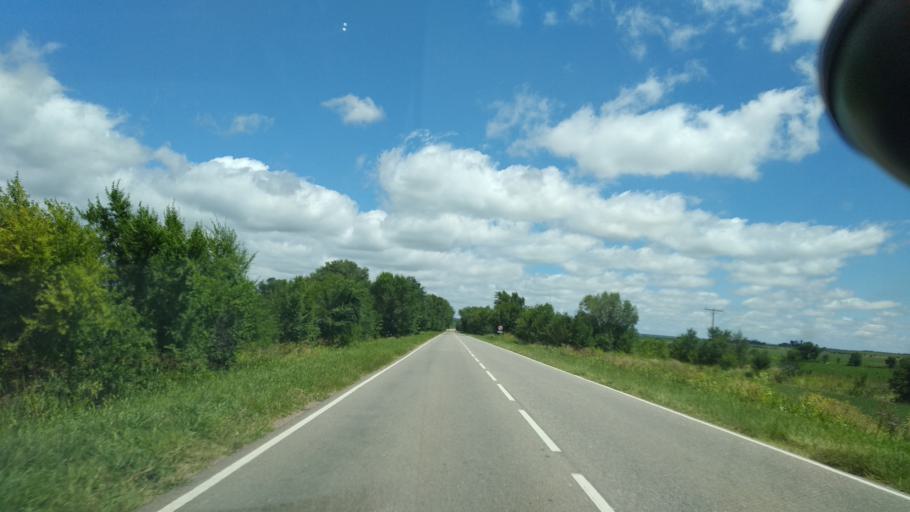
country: AR
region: Cordoba
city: Villa Cura Brochero
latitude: -31.6733
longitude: -65.0915
